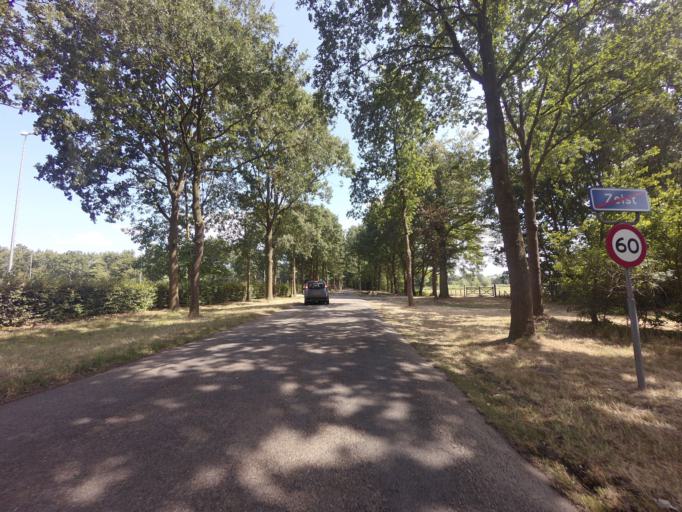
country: NL
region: Utrecht
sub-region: Gemeente Zeist
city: Zeist
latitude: 52.0751
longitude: 5.2304
